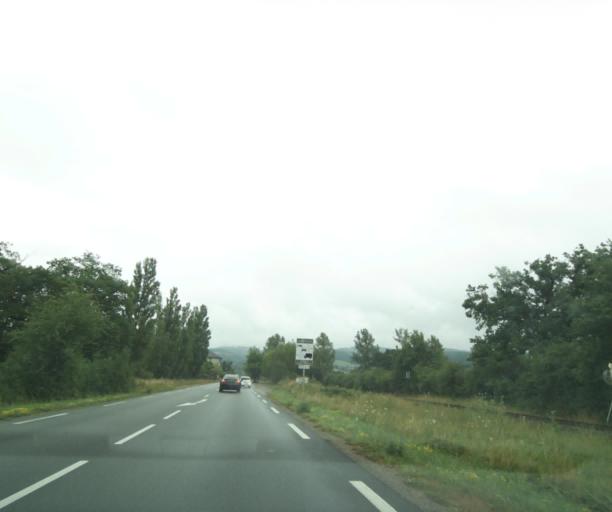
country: FR
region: Midi-Pyrenees
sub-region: Departement de l'Aveyron
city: La Loubiere
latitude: 44.3916
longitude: 2.6903
